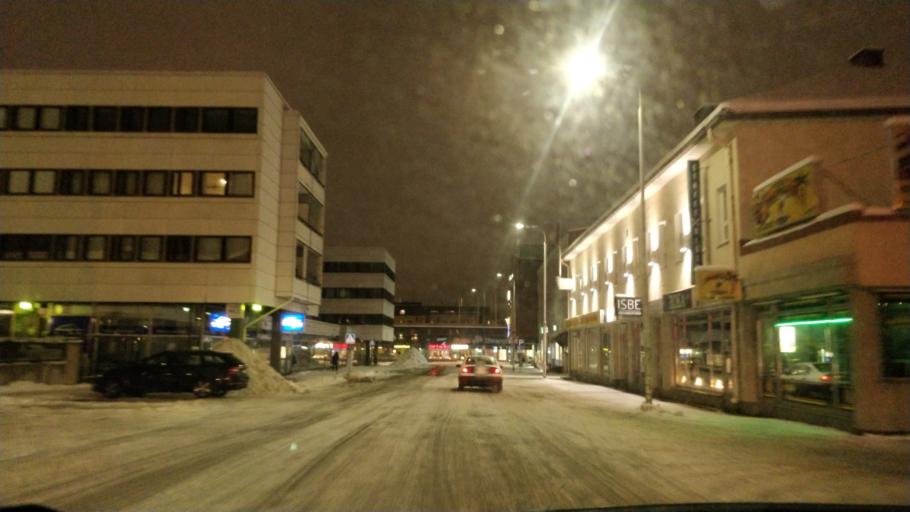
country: FI
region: Lapland
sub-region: Rovaniemi
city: Rovaniemi
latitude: 66.5020
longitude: 25.7249
